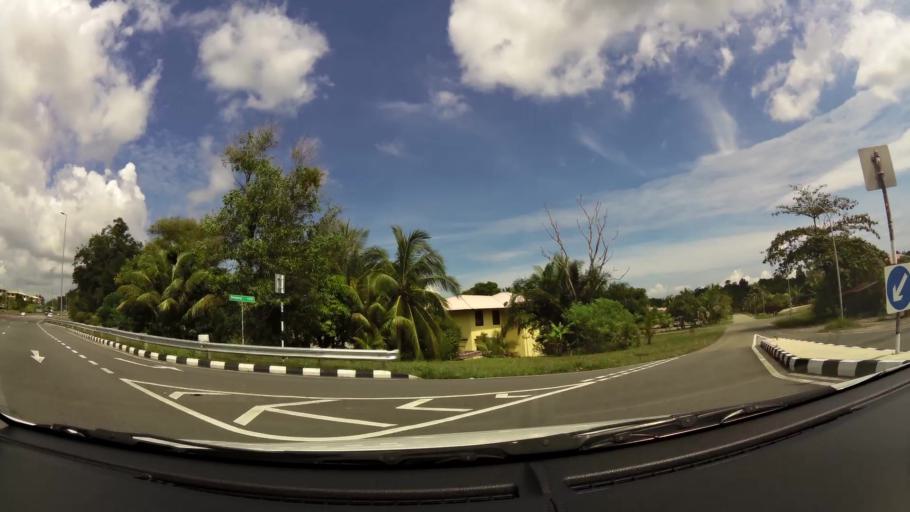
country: BN
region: Brunei and Muara
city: Bandar Seri Begawan
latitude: 4.9346
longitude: 114.8964
